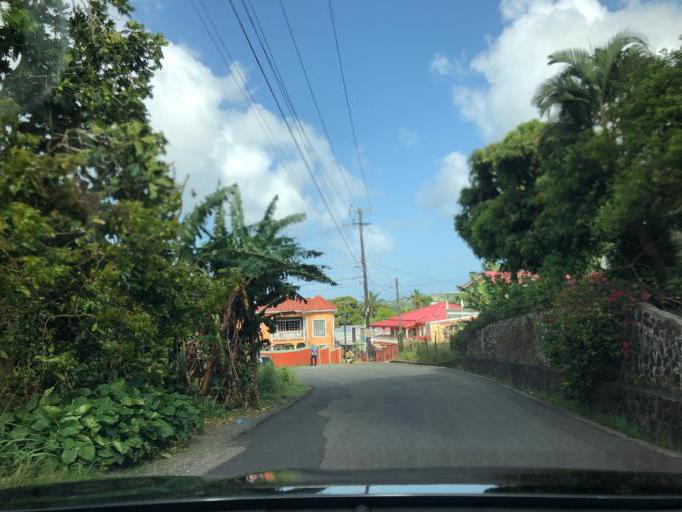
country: LC
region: Castries Quarter
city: Bisee
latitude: 14.0032
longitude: -60.9488
